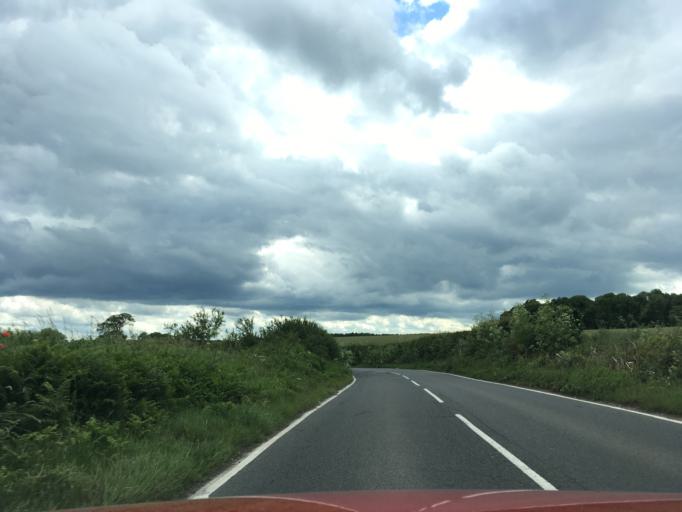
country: GB
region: England
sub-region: Central Bedfordshire
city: Woburn
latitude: 51.9813
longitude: -0.6376
